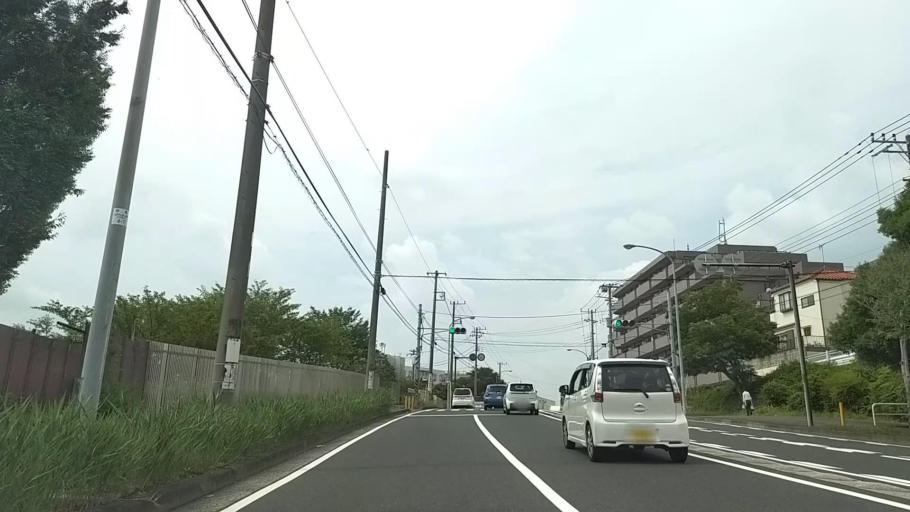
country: JP
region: Kanagawa
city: Minami-rinkan
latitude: 35.5016
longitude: 139.5423
